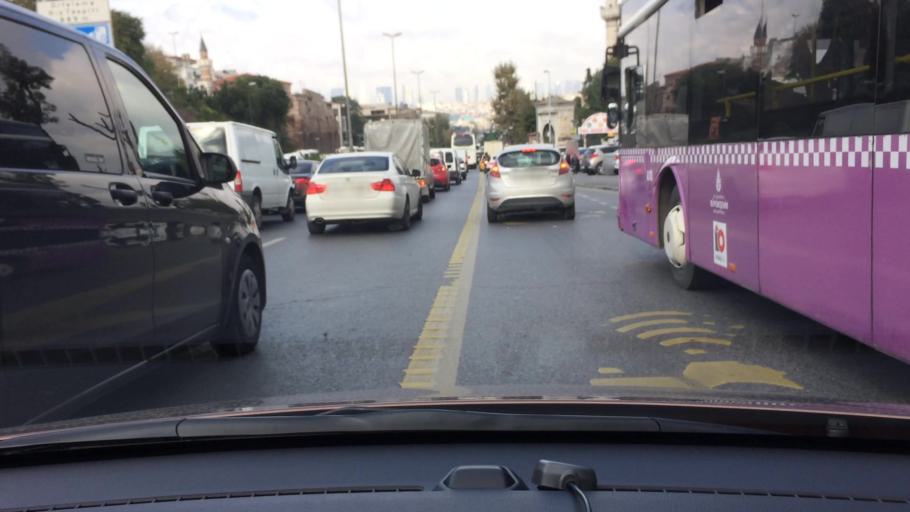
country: TR
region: Istanbul
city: Istanbul
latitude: 41.0184
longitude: 28.9579
